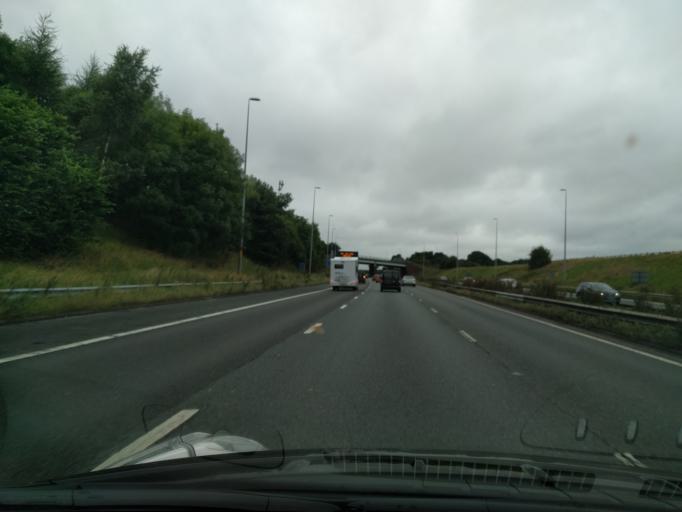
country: GB
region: England
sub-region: St. Helens
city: Newton-le-Willows
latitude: 53.4439
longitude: -2.5885
